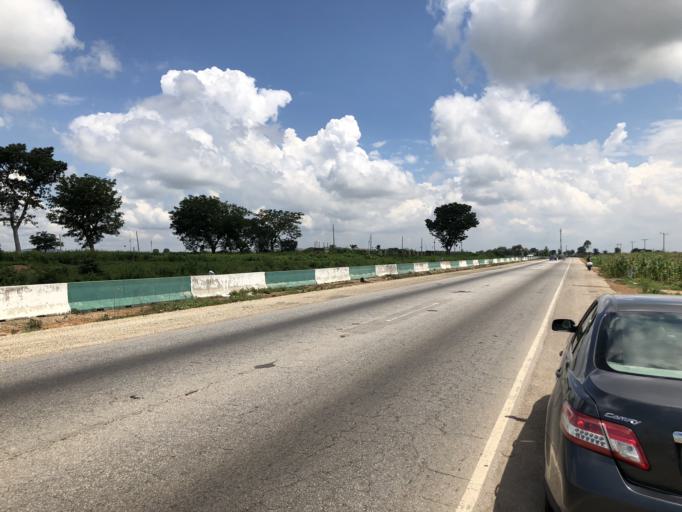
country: NG
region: Nassarawa
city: Karu
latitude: 8.9269
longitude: 7.6897
